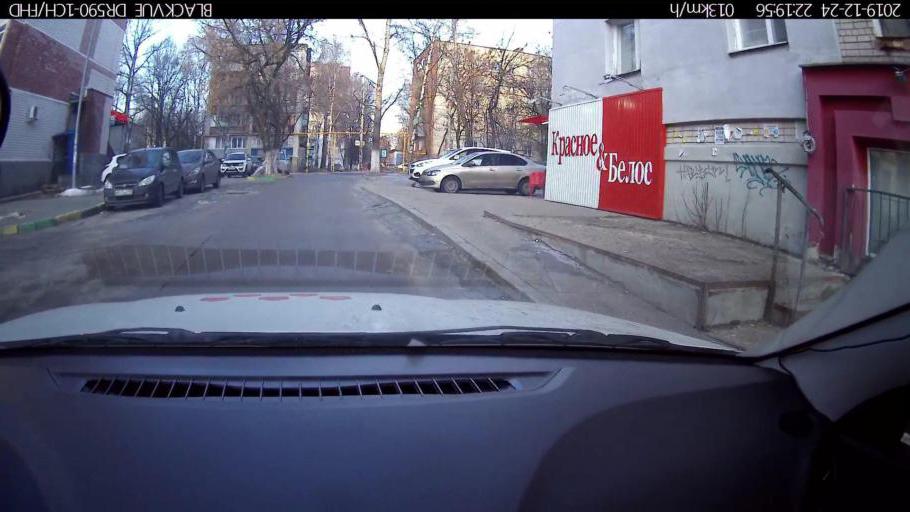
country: RU
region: Nizjnij Novgorod
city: Nizhniy Novgorod
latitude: 56.2373
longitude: 43.9670
